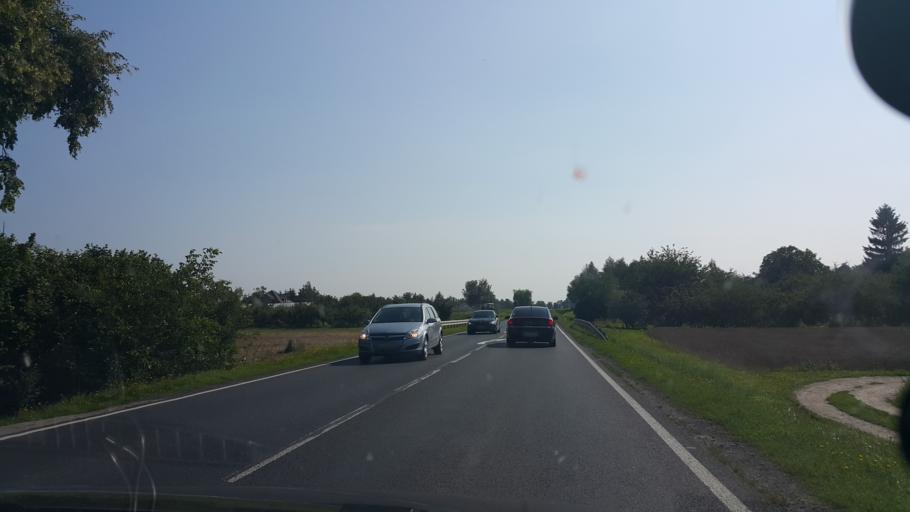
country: PL
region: Lublin Voivodeship
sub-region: Powiat leczynski
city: Spiczyn
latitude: 51.3018
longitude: 22.8064
